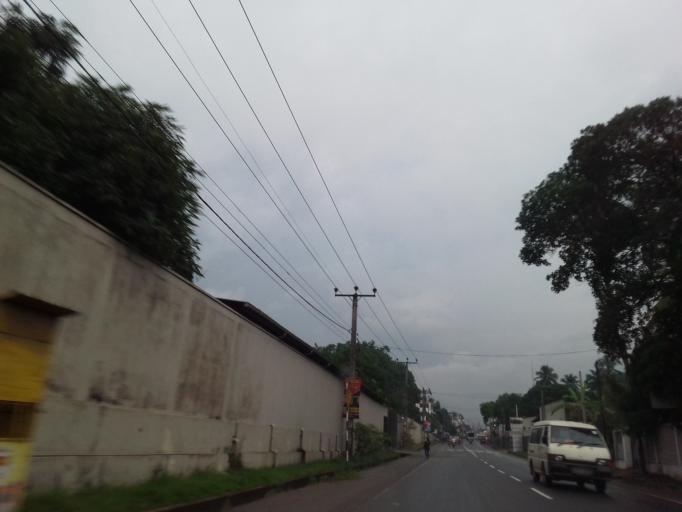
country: LK
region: Western
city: Battaramulla South
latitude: 6.8905
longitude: 79.9649
